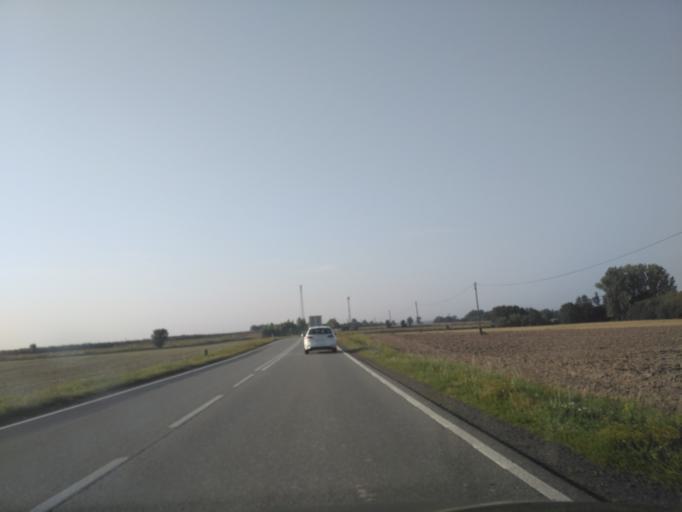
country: PL
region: Lublin Voivodeship
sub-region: Powiat janowski
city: Modliborzyce
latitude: 50.7741
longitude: 22.3247
